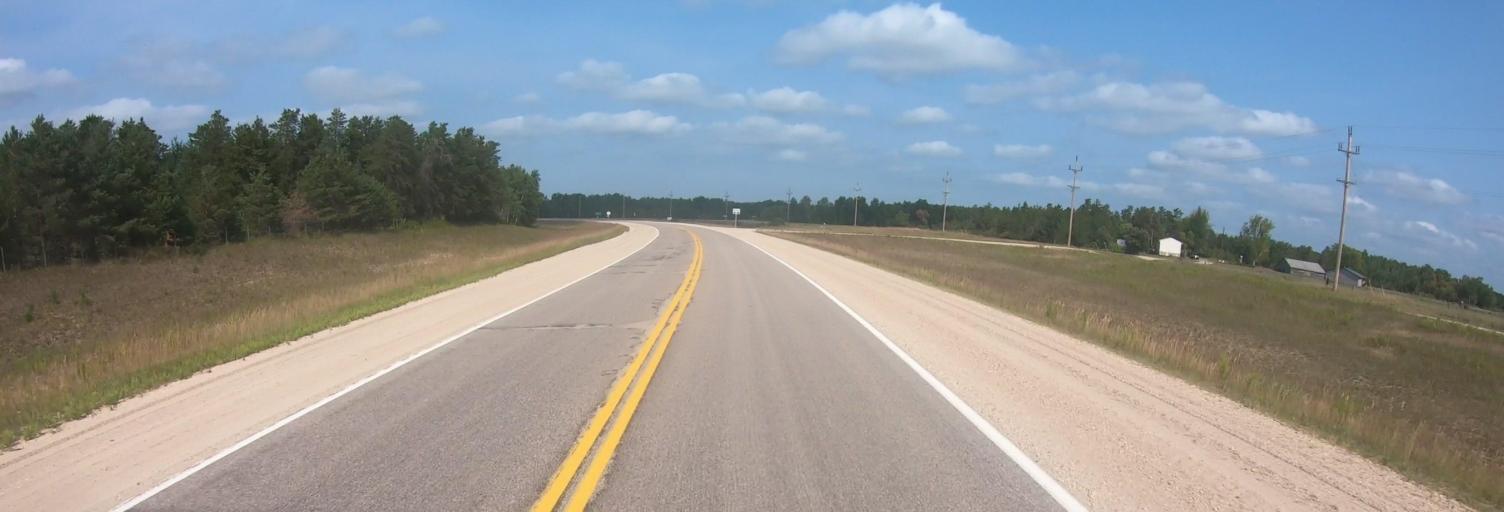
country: CA
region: Manitoba
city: La Broquerie
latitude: 49.2641
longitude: -96.3629
